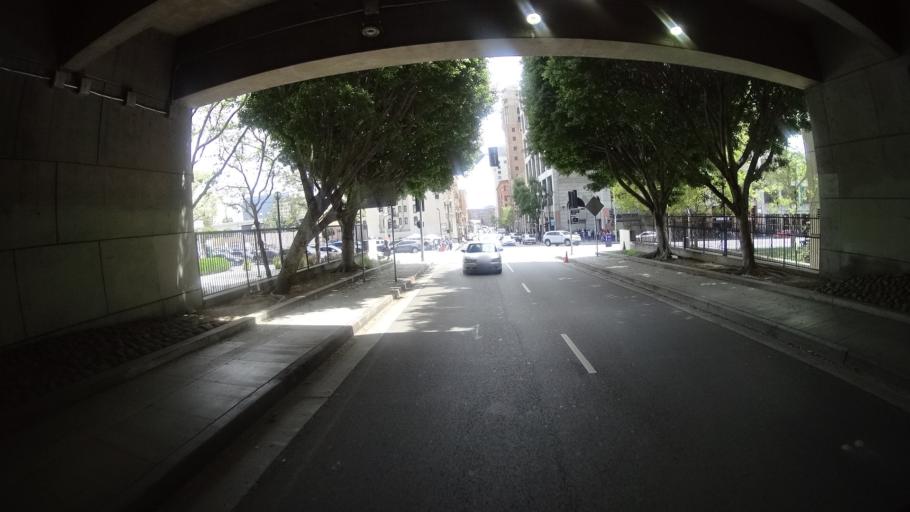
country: US
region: California
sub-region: Los Angeles County
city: Los Angeles
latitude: 34.0517
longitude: -118.2496
